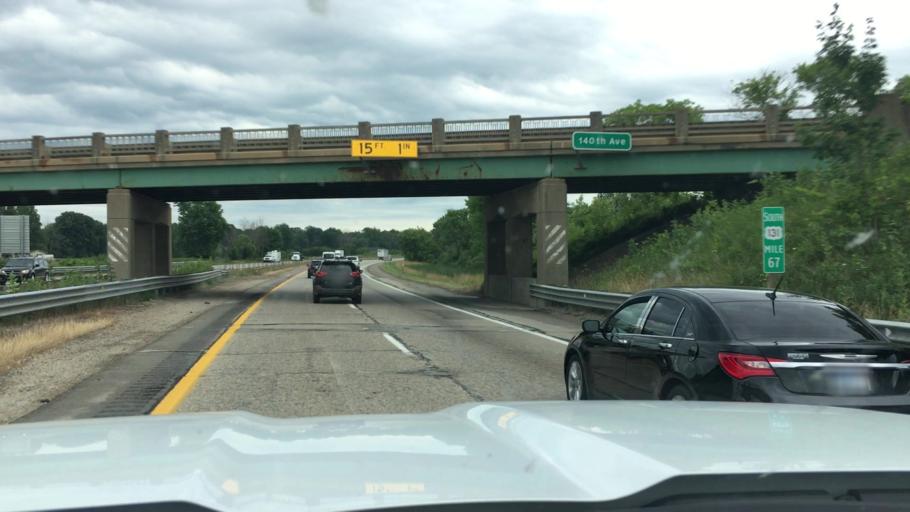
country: US
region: Michigan
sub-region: Allegan County
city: Wayland
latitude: 42.7105
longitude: -85.6617
